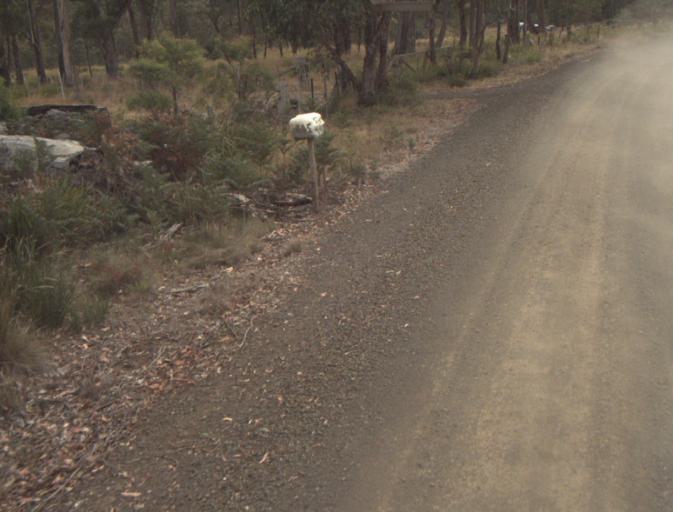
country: AU
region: Tasmania
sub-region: Northern Midlands
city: Evandale
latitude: -41.5206
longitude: 147.4395
